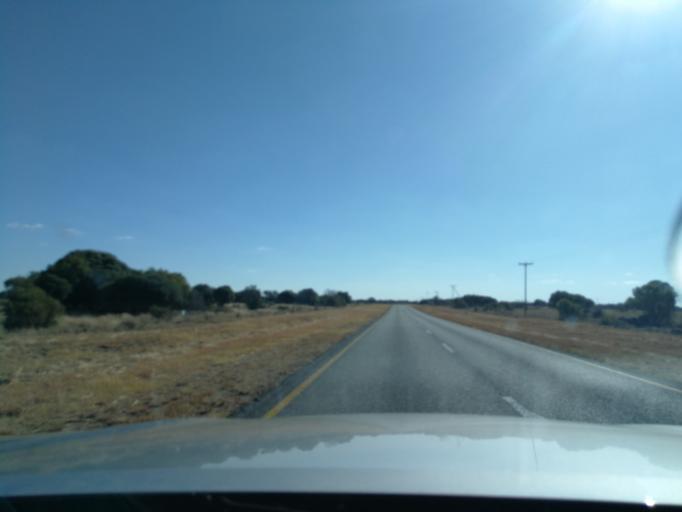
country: ZA
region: North-West
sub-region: Ngaka Modiri Molema District Municipality
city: Zeerust
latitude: -25.7791
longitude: 26.0018
